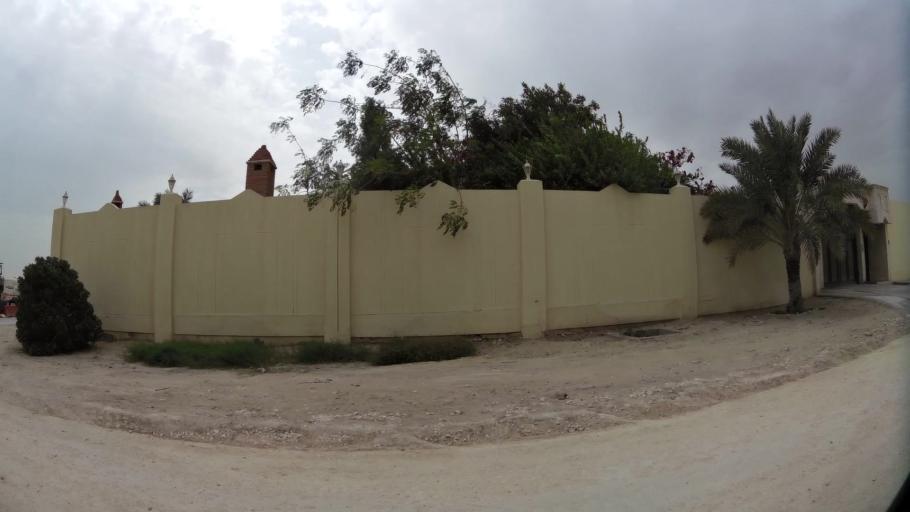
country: QA
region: Baladiyat ar Rayyan
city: Ar Rayyan
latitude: 25.3445
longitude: 51.4718
